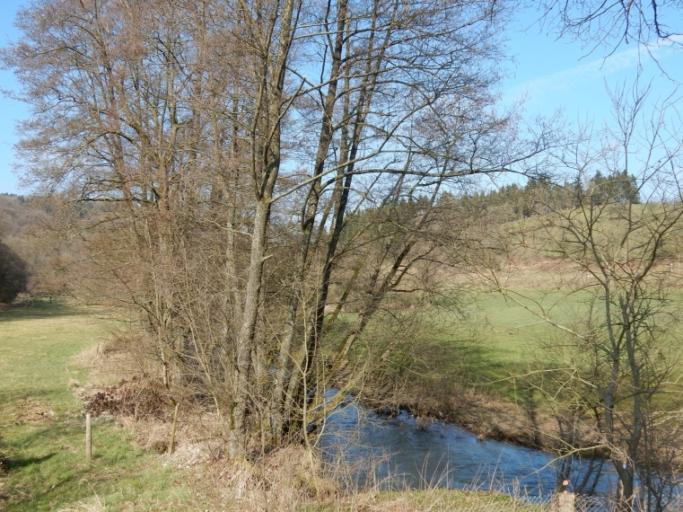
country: LU
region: Diekirch
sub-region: Canton de Wiltz
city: Winseler
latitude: 49.9917
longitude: 5.8563
